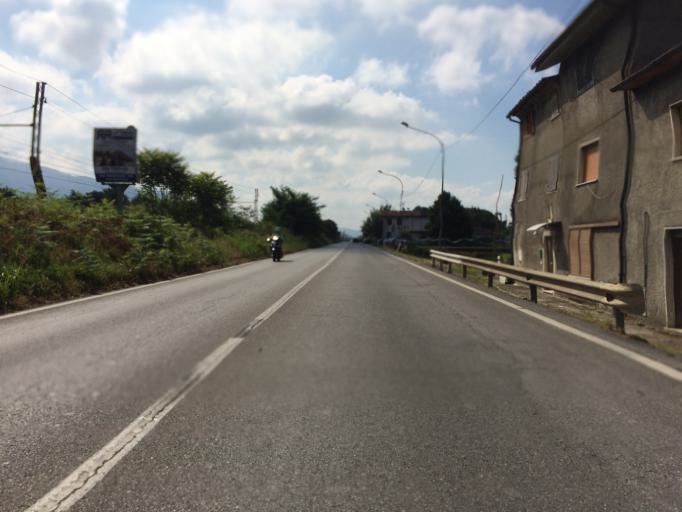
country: IT
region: Tuscany
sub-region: Provincia di Lucca
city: Strettoia
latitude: 43.9875
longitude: 10.1857
